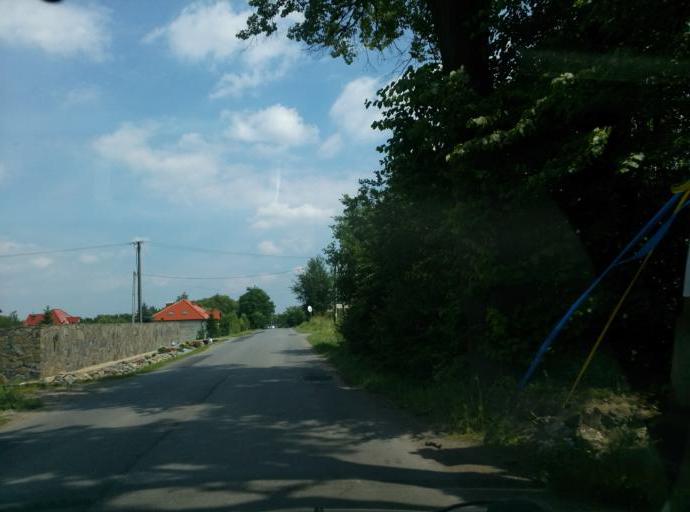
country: PL
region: Lesser Poland Voivodeship
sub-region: Powiat krakowski
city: Mogilany
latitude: 49.9442
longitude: 19.8695
